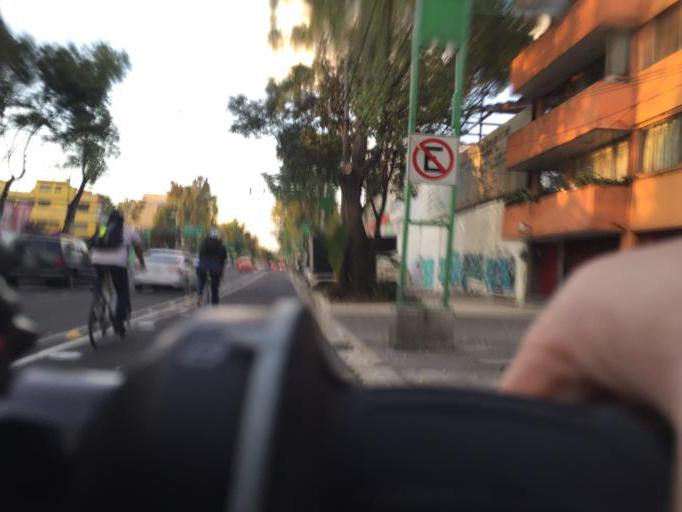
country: MX
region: Mexico City
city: Colonia Nativitas
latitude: 19.3710
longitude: -99.1497
